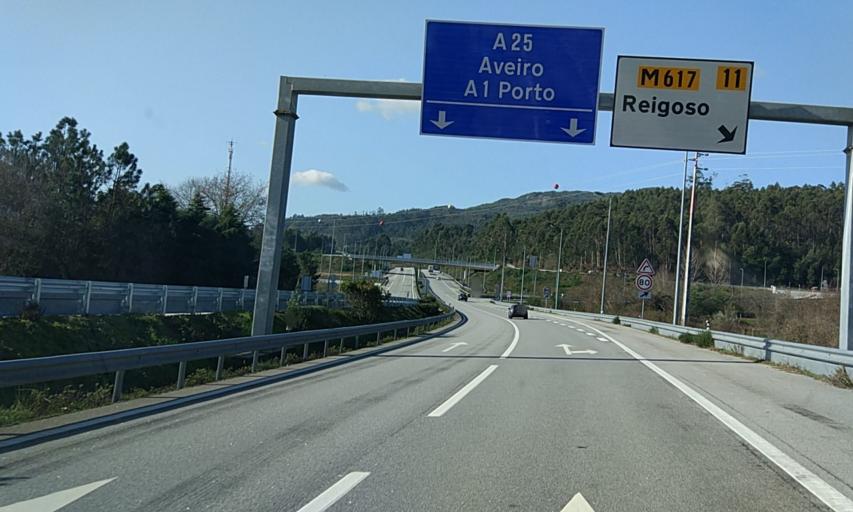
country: PT
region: Viseu
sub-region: Oliveira de Frades
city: Oliveira de Frades
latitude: 40.6831
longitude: -8.2635
